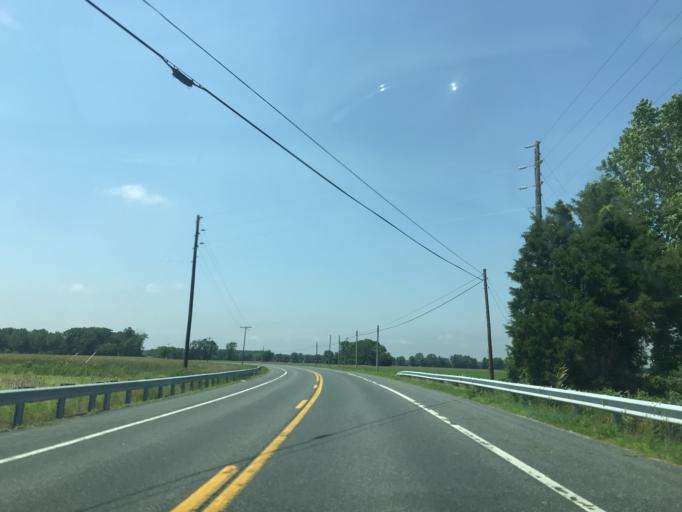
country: US
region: Maryland
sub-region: Caroline County
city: Federalsburg
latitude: 38.6439
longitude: -75.7131
